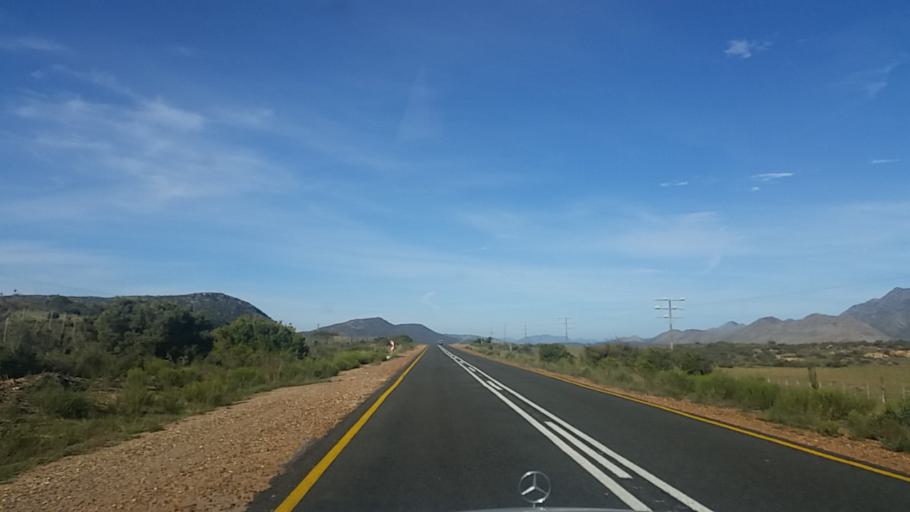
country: ZA
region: Western Cape
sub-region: Eden District Municipality
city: George
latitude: -33.7819
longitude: 22.6773
